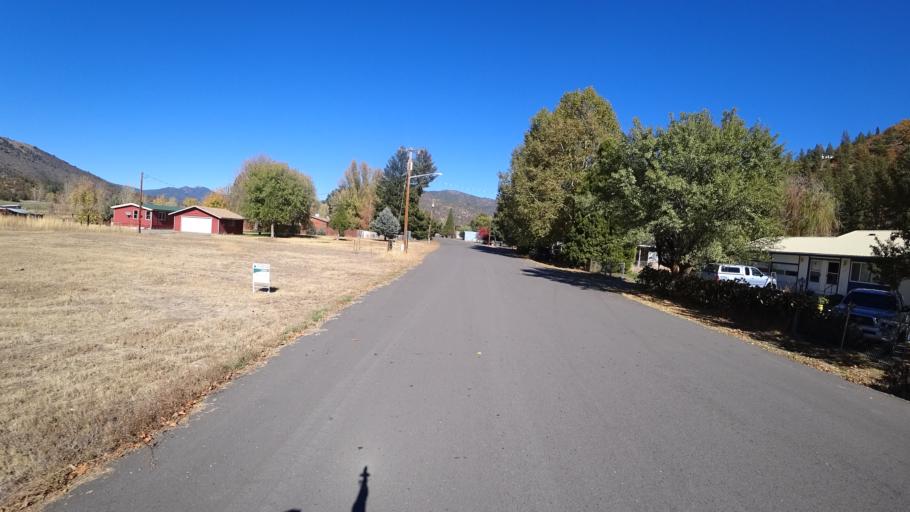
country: US
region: California
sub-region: Siskiyou County
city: Yreka
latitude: 41.6172
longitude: -122.8360
